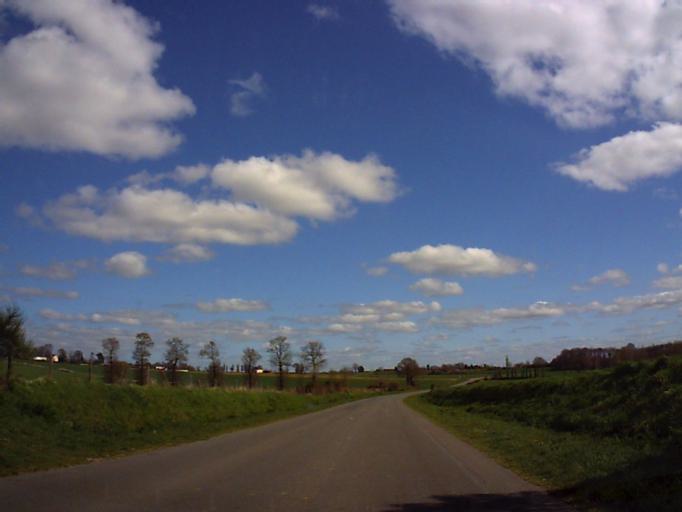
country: FR
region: Brittany
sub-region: Departement d'Ille-et-Vilaine
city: Saint-Meen-le-Grand
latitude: 48.1727
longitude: -2.1664
